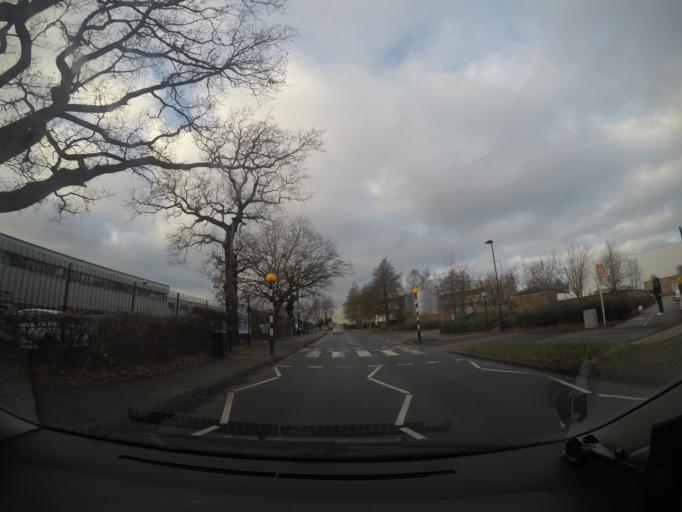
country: GB
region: England
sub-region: City of York
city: Huntington
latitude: 53.9858
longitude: -1.0500
